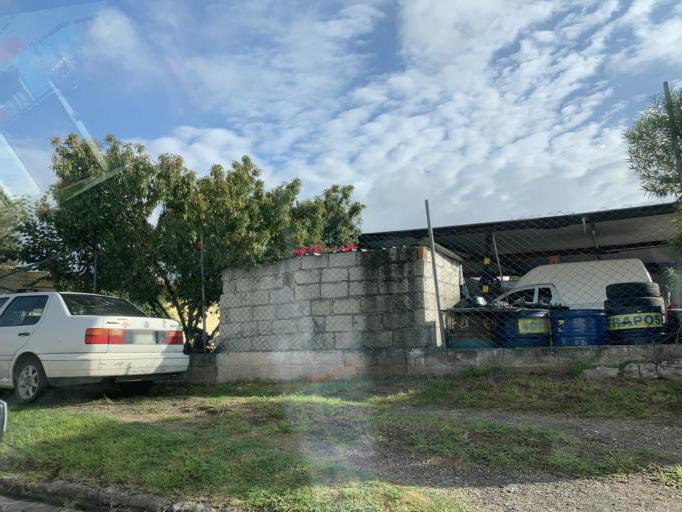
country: MX
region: Puebla
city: San Andres Cholula
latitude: 19.0526
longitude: -98.2913
